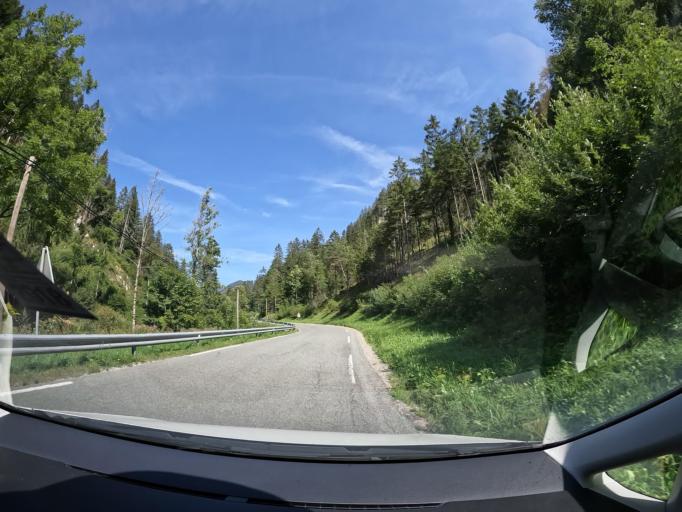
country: SI
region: Jesenice
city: Koroska Bela
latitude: 46.4766
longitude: 14.1044
